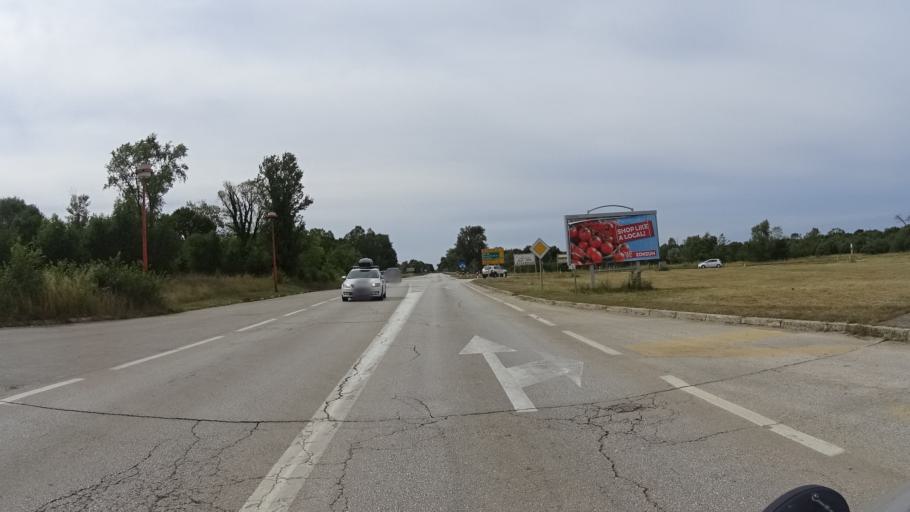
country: HR
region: Istarska
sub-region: Grad Rovinj
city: Rovinj
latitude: 45.1103
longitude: 13.7678
